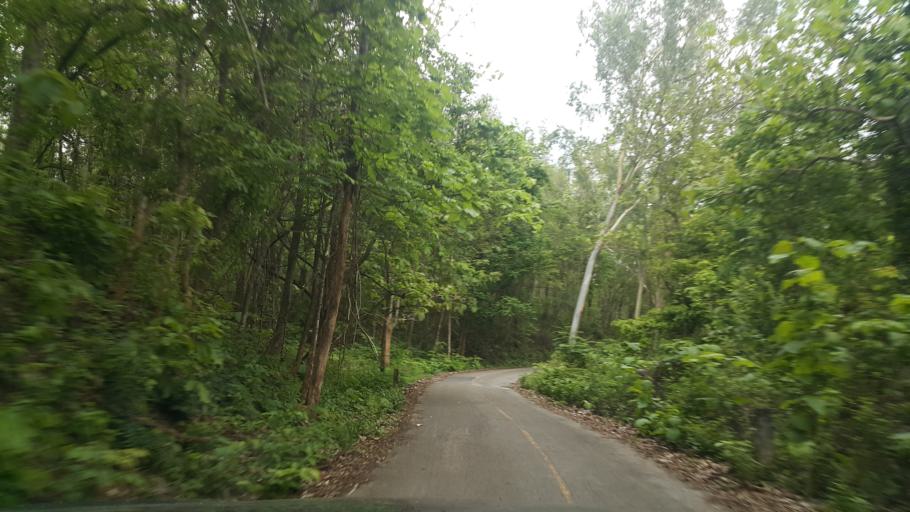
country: TH
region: Chiang Mai
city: Mae On
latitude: 18.7225
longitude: 99.2324
